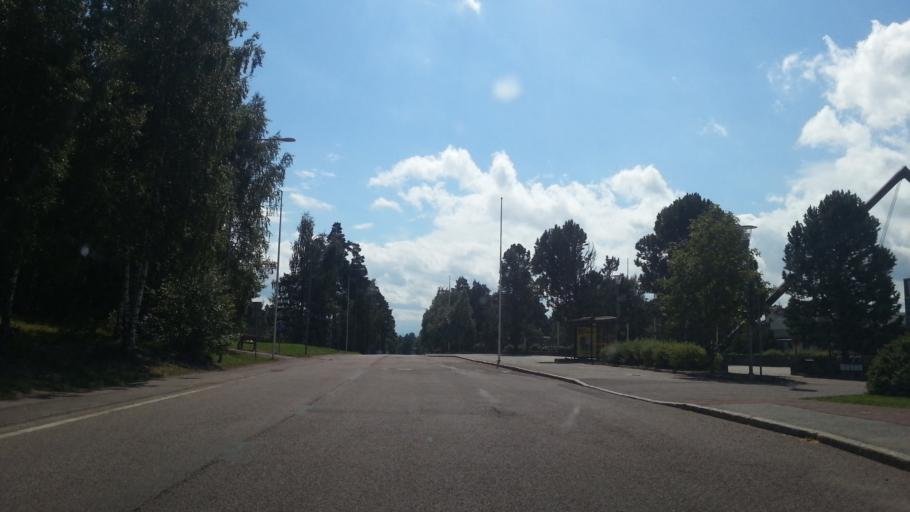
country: SE
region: Dalarna
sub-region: Faluns Kommun
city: Falun
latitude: 60.6187
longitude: 15.6584
